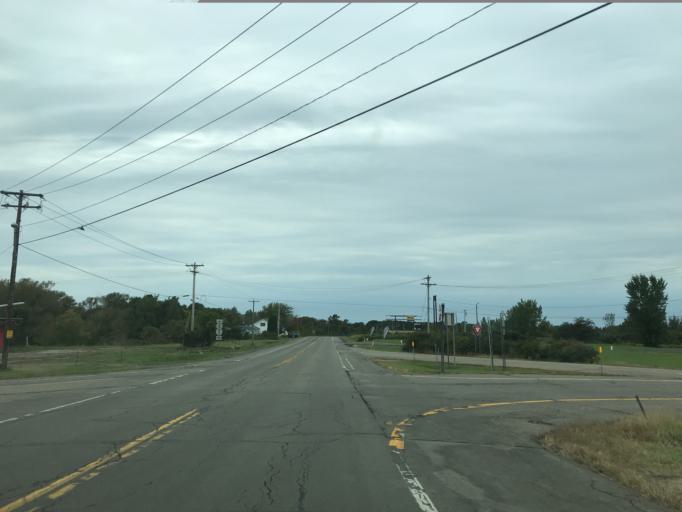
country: US
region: Pennsylvania
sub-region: Erie County
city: North East
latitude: 42.2632
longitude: -79.7459
